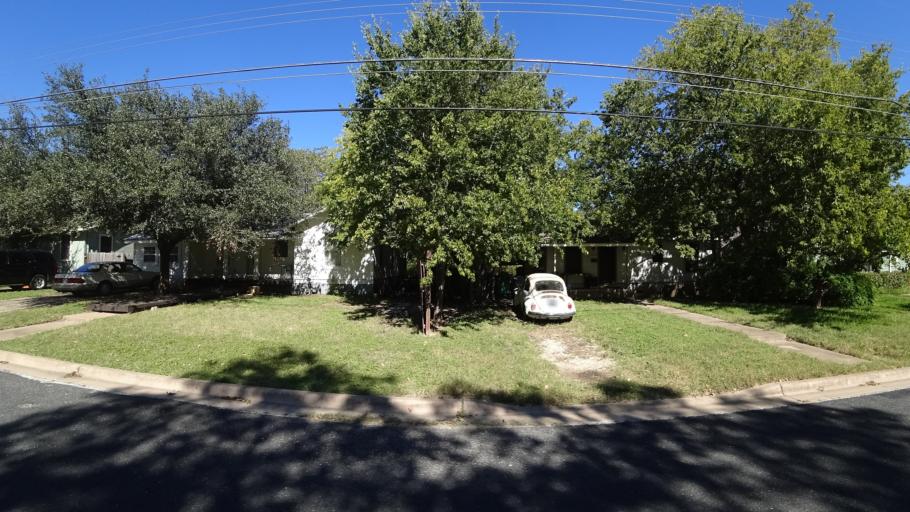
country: US
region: Texas
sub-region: Travis County
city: Austin
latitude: 30.3356
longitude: -97.7376
